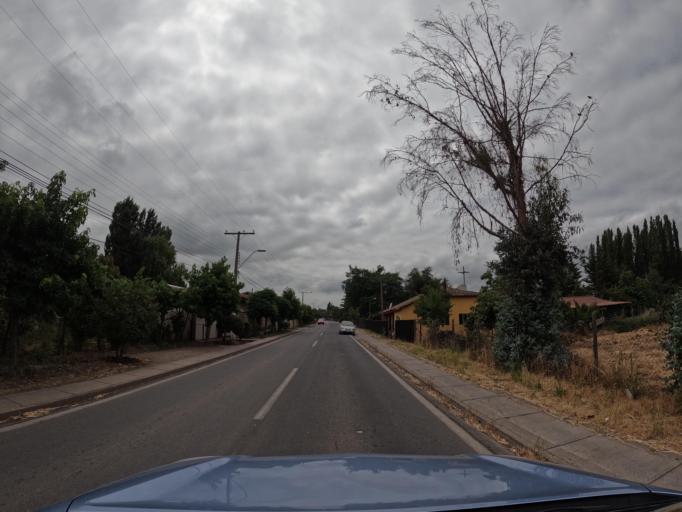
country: CL
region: Maule
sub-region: Provincia de Curico
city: Teno
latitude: -34.7610
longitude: -71.1995
